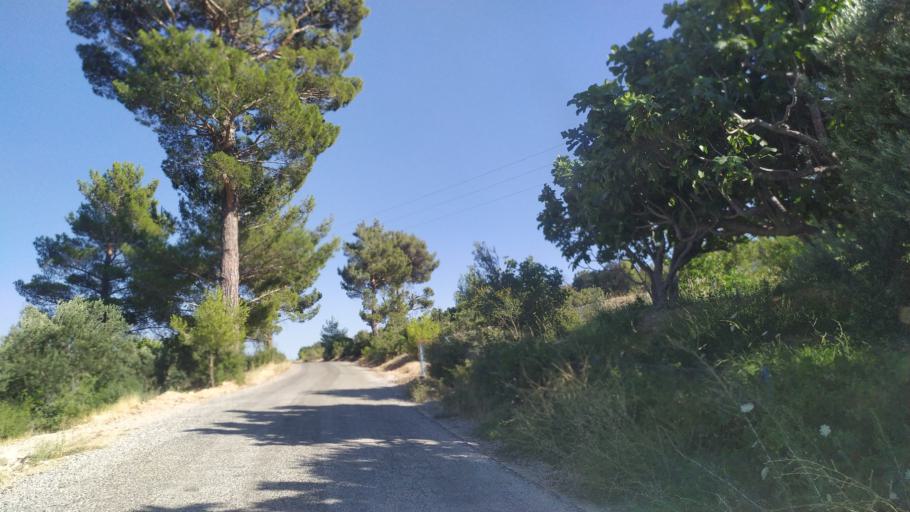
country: TR
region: Mersin
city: Mut
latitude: 36.7009
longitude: 33.4785
